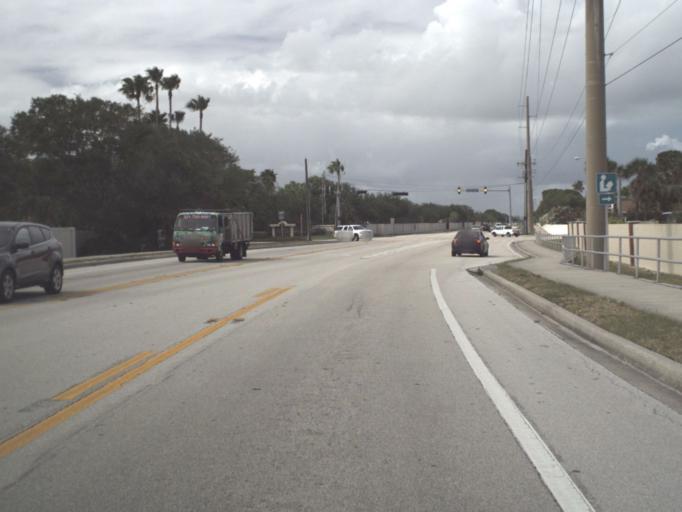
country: US
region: Florida
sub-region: Brevard County
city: Satellite Beach
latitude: 28.1637
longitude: -80.6057
